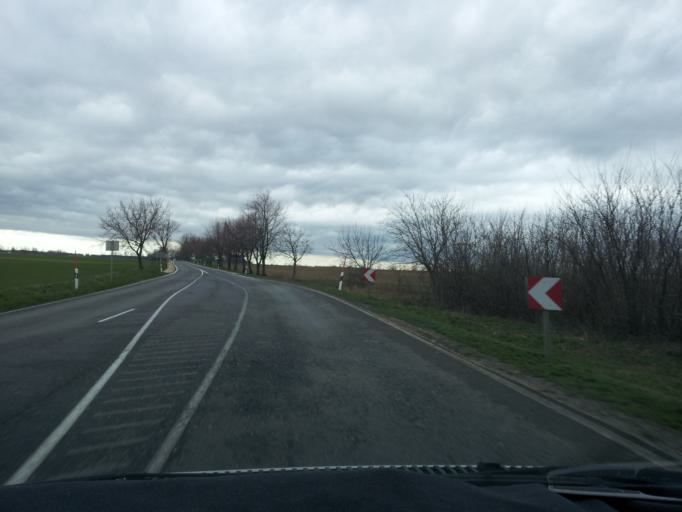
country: HU
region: Gyor-Moson-Sopron
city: Beled
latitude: 47.4567
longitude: 17.0908
